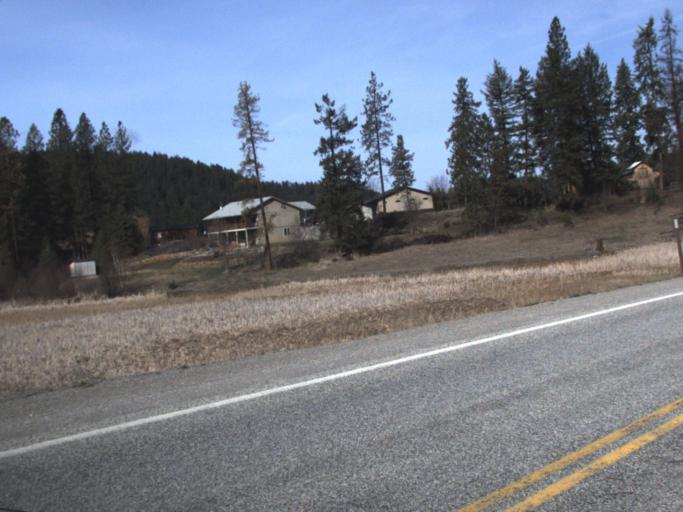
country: US
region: Washington
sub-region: Stevens County
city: Colville
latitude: 48.5157
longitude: -117.8064
